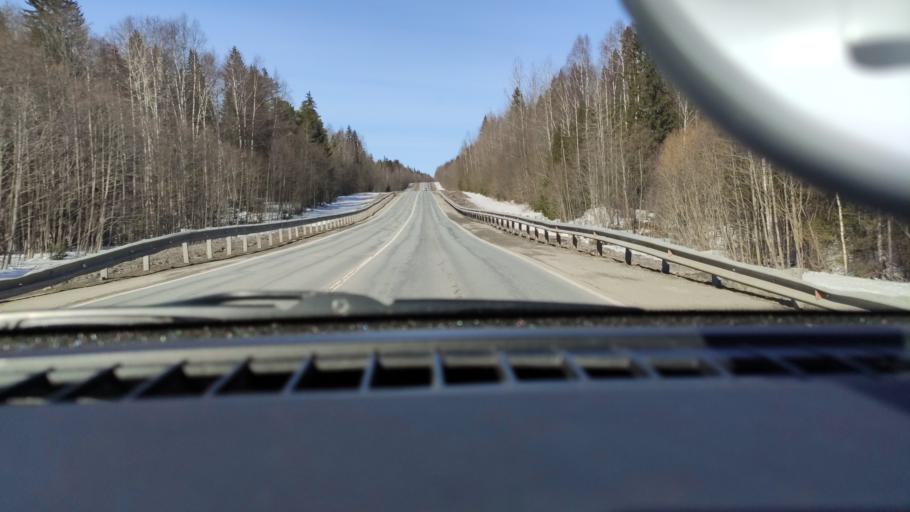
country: RU
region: Perm
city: Perm
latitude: 58.1620
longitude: 56.2443
